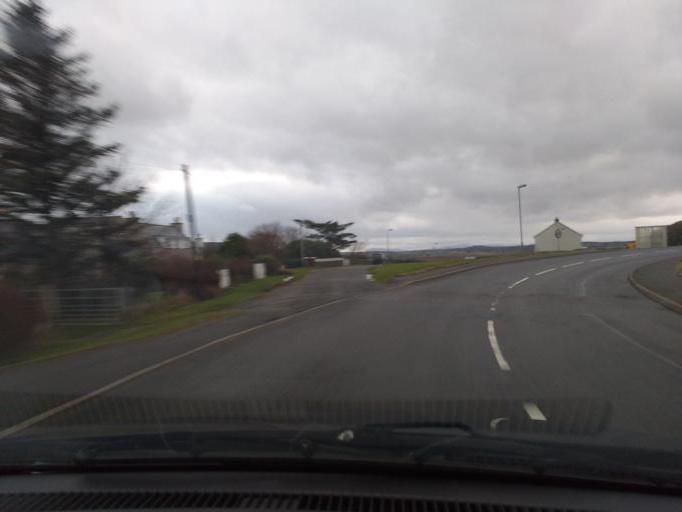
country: GB
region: Scotland
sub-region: Eilean Siar
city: Isle of Lewis
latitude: 58.2414
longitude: -6.3507
